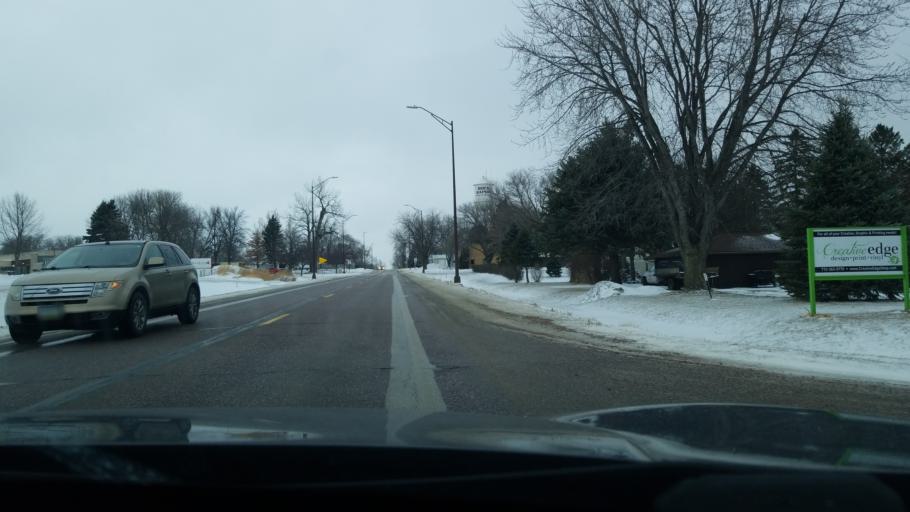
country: US
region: Iowa
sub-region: Lyon County
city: Rock Rapids
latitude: 43.4229
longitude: -96.1757
